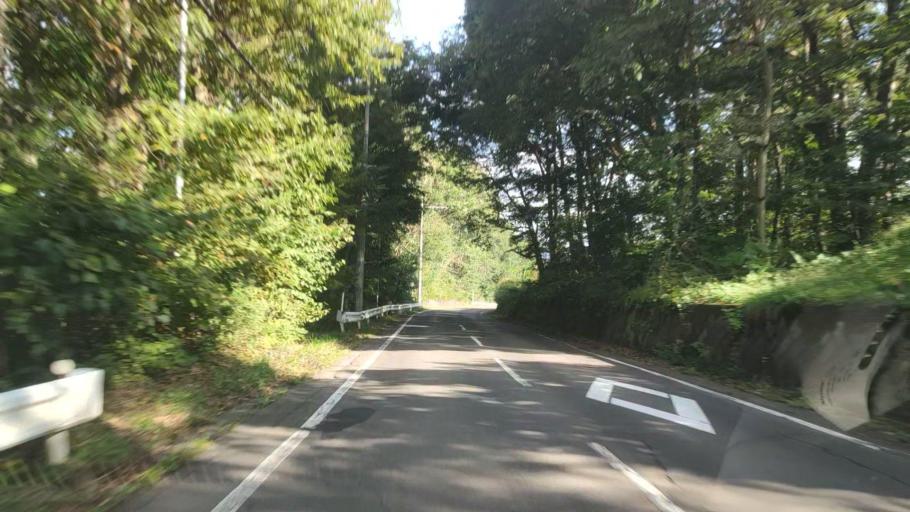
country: JP
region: Nagano
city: Suzaka
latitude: 36.5637
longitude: 138.5551
